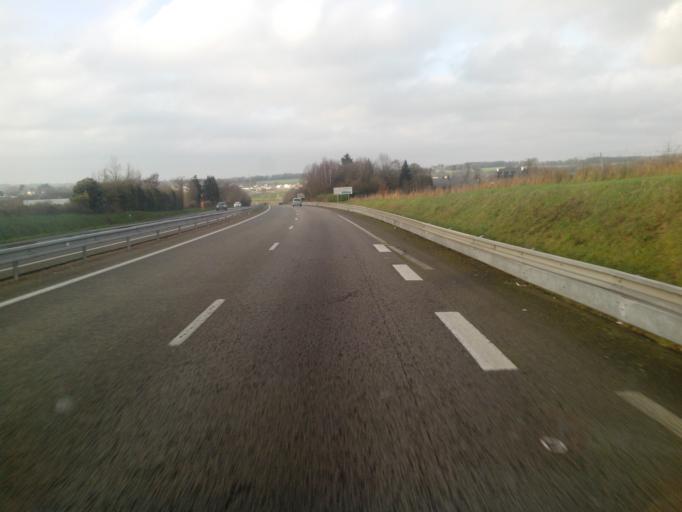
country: FR
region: Brittany
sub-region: Departement du Morbihan
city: Josselin
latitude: 47.9565
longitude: -2.5325
